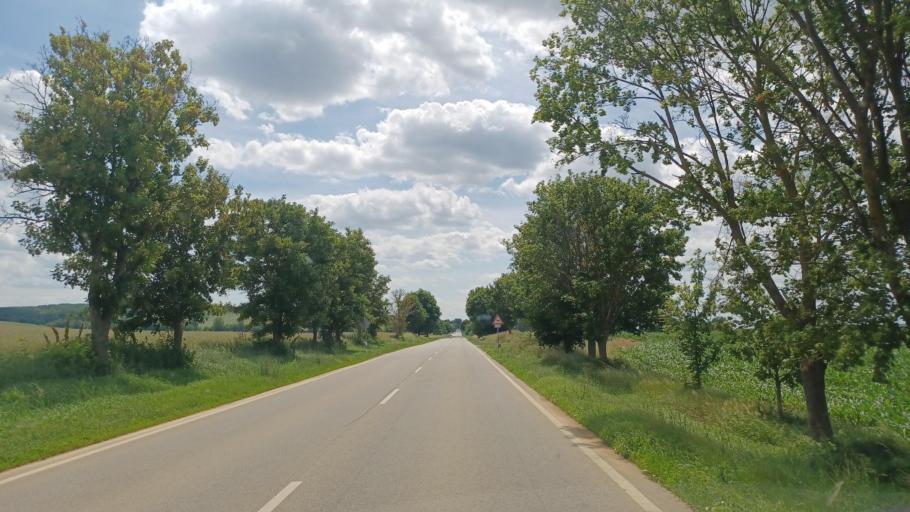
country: HU
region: Tolna
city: Simontornya
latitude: 46.7315
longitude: 18.4989
